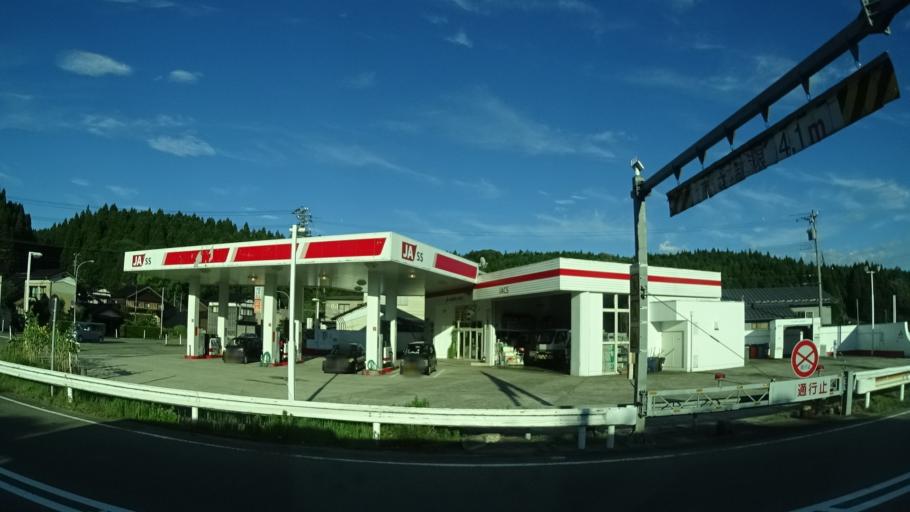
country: JP
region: Ishikawa
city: Nanao
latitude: 37.2436
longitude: 136.8990
